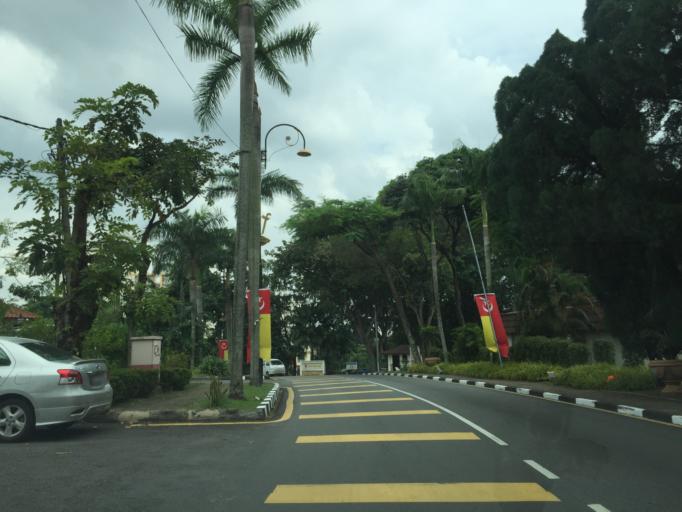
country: MY
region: Selangor
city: Klang
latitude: 3.0381
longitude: 101.4483
